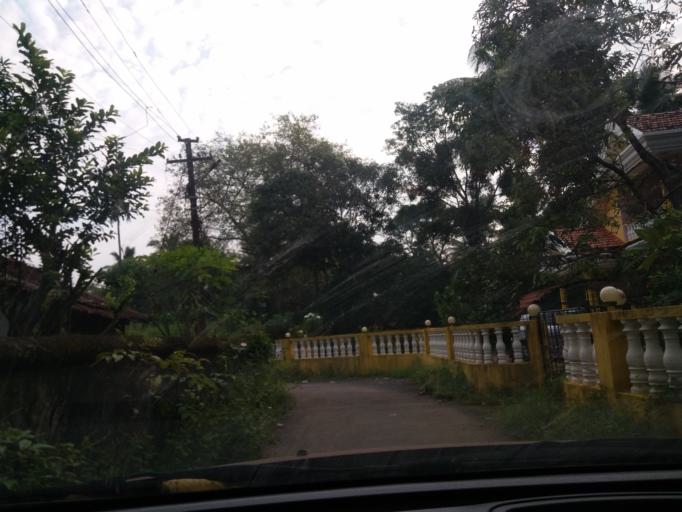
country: IN
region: Goa
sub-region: South Goa
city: Varca
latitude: 15.2296
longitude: 73.9512
